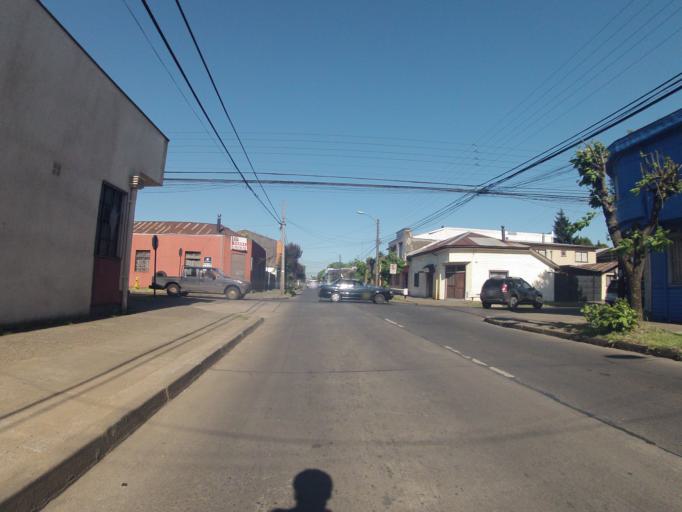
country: CL
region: Araucania
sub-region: Provincia de Cautin
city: Temuco
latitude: -38.7347
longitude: -72.5938
